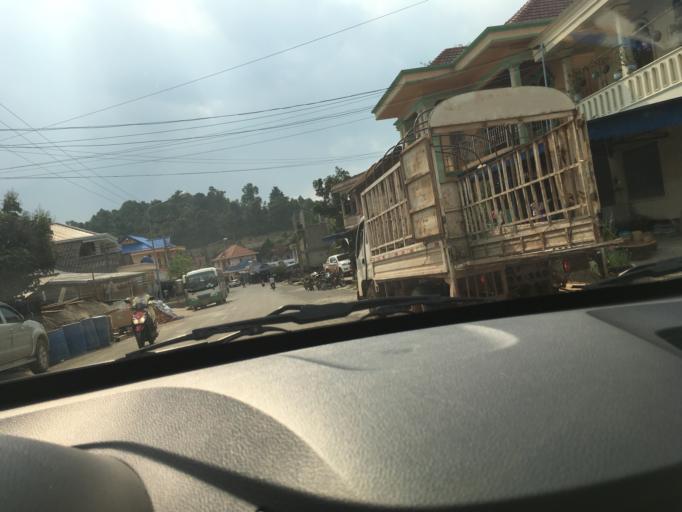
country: LA
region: Phongsali
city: Phongsali
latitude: 21.6831
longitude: 102.1017
